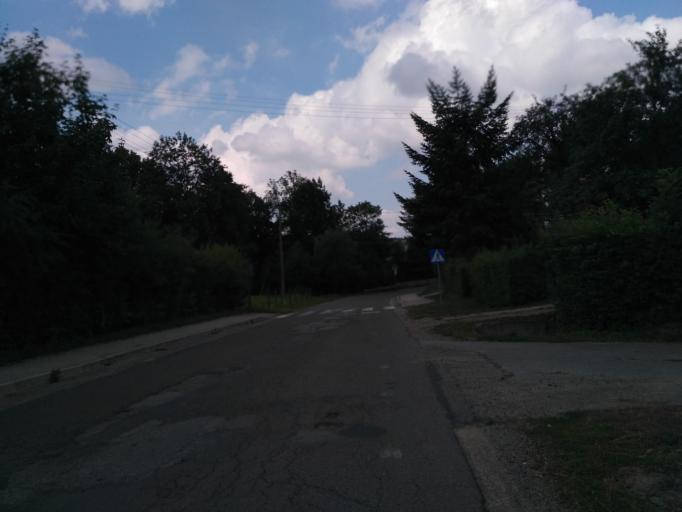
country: PL
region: Subcarpathian Voivodeship
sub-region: Powiat krosnienski
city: Iwonicz-Zdroj
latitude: 49.5765
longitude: 21.7530
